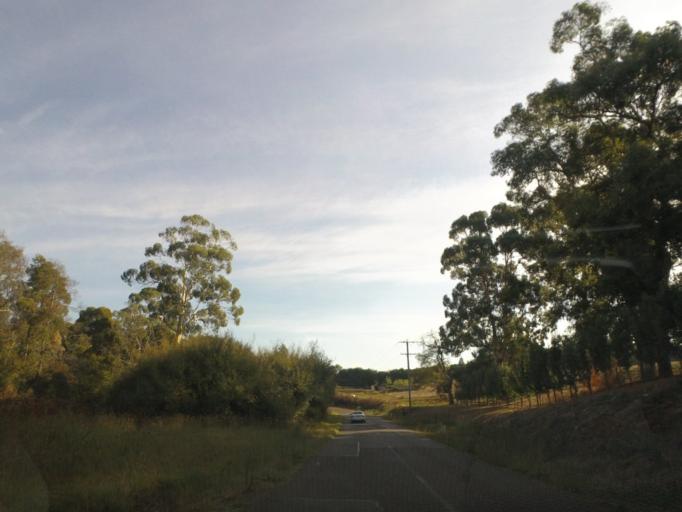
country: AU
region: Victoria
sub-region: Yarra Ranges
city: Mount Evelyn
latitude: -37.7989
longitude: 145.4445
